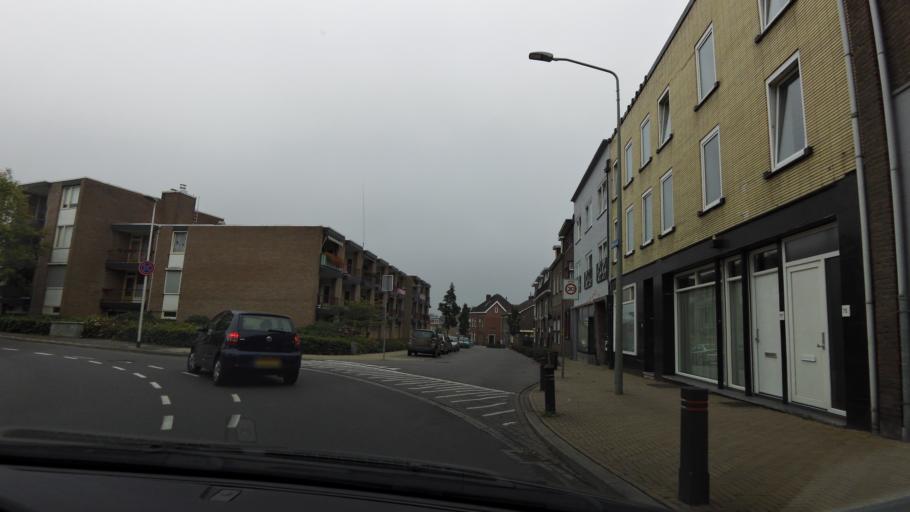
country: NL
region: Limburg
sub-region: Gemeente Heerlen
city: Hoensbroek
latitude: 50.9227
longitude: 5.9289
